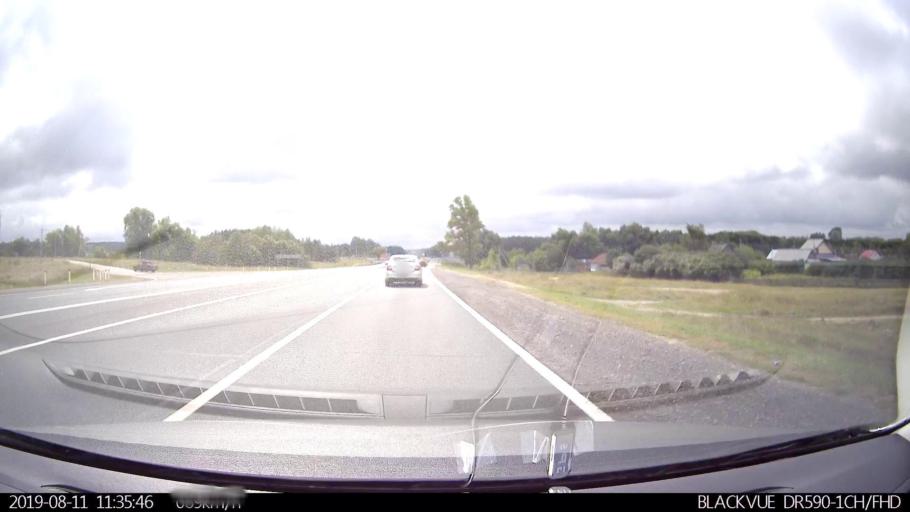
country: RU
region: Ulyanovsk
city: Silikatnyy
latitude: 54.0029
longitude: 48.2207
